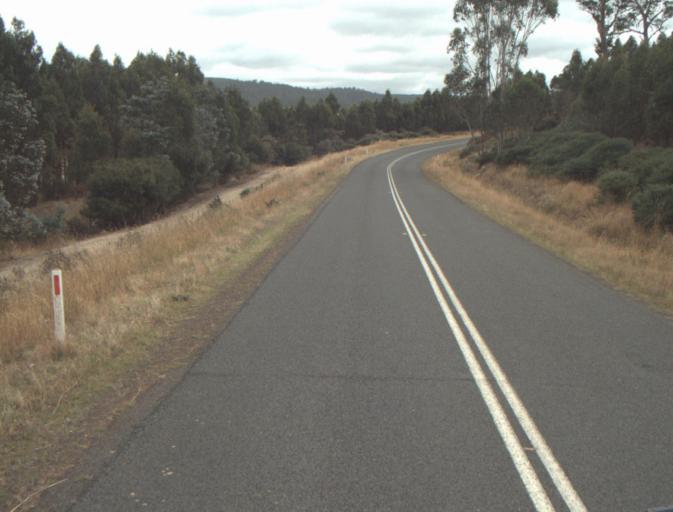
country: AU
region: Tasmania
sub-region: Northern Midlands
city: Evandale
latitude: -41.4956
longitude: 147.4970
